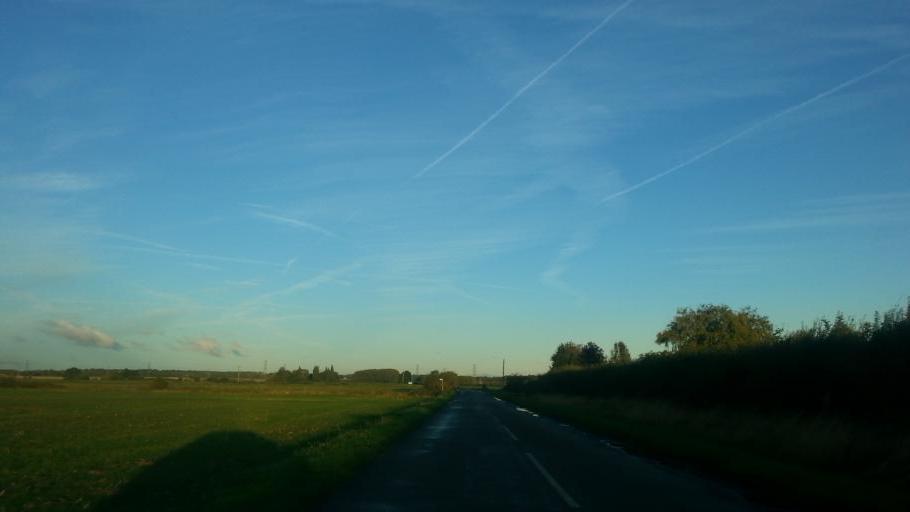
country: GB
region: England
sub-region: Nottinghamshire
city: Farndon
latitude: 53.0067
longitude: -0.8390
